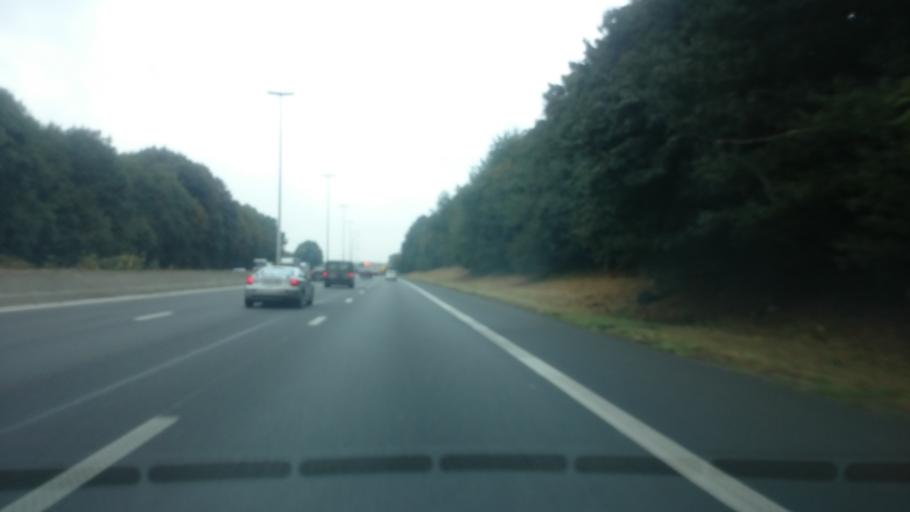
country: BE
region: Wallonia
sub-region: Province de Namur
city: Namur
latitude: 50.5070
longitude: 4.8399
